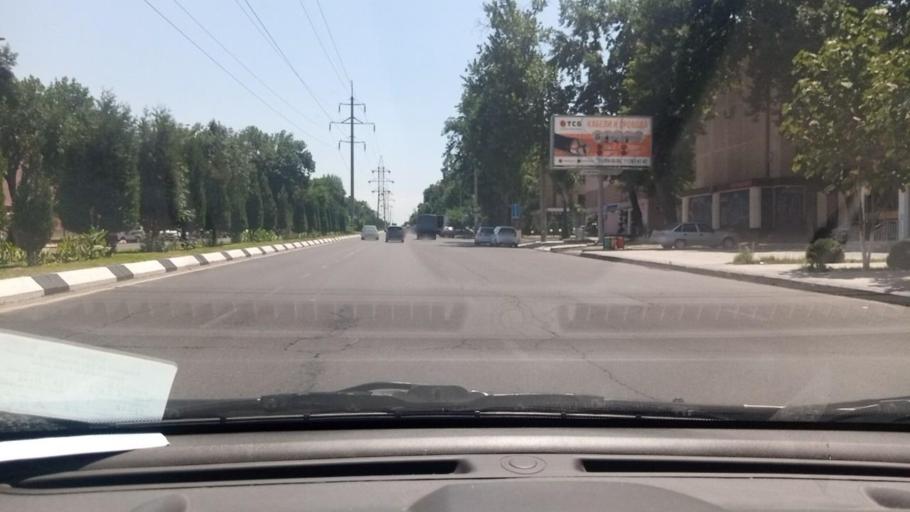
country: UZ
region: Toshkent Shahri
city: Tashkent
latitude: 41.2956
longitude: 69.1942
